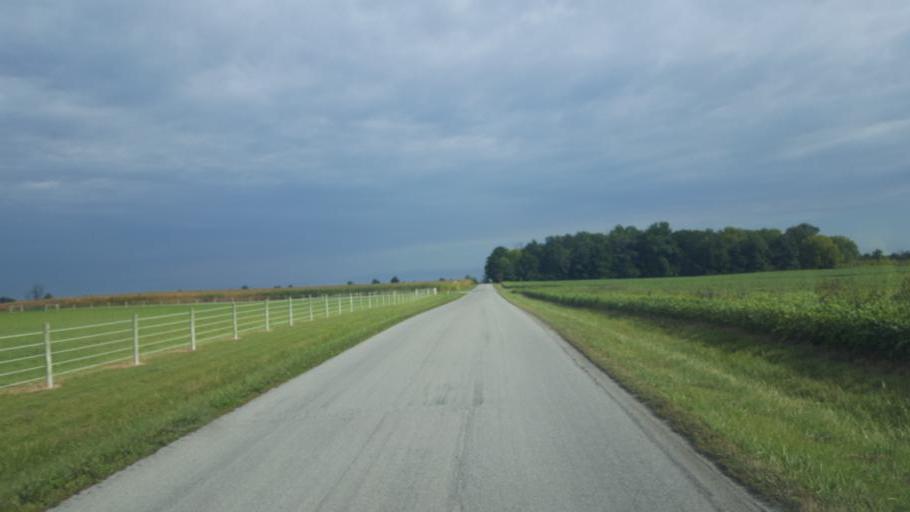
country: US
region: Ohio
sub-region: Marion County
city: Marion
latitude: 40.7232
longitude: -83.1307
